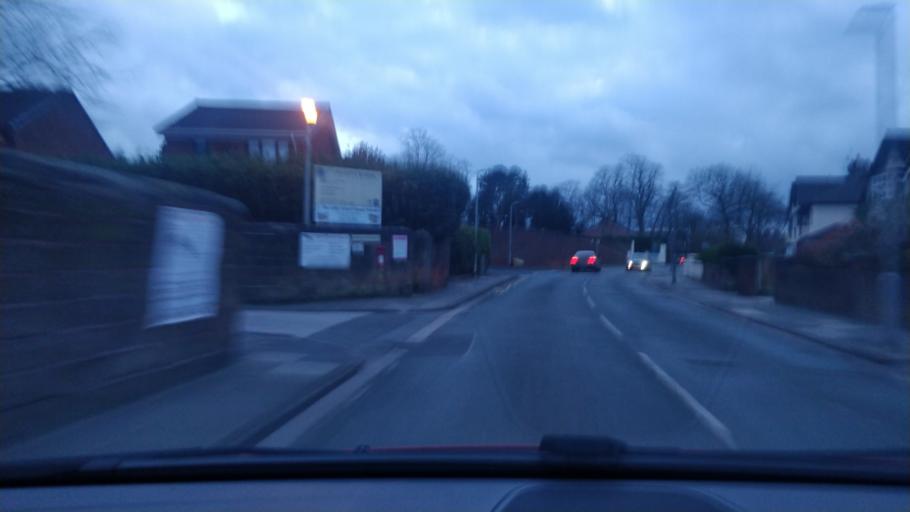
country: GB
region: England
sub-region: Knowsley
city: Knowsley
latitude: 53.4266
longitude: -2.8864
